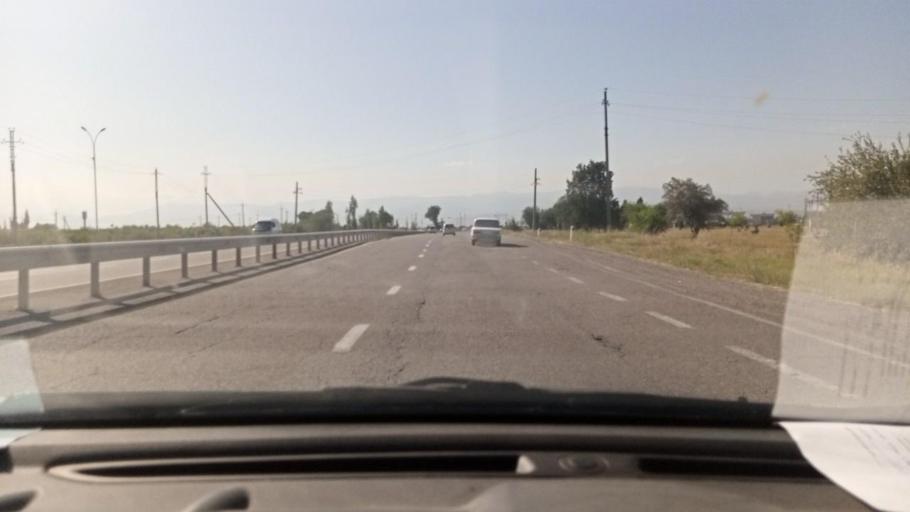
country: UZ
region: Toshkent
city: Ohangaron
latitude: 40.9319
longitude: 69.5925
